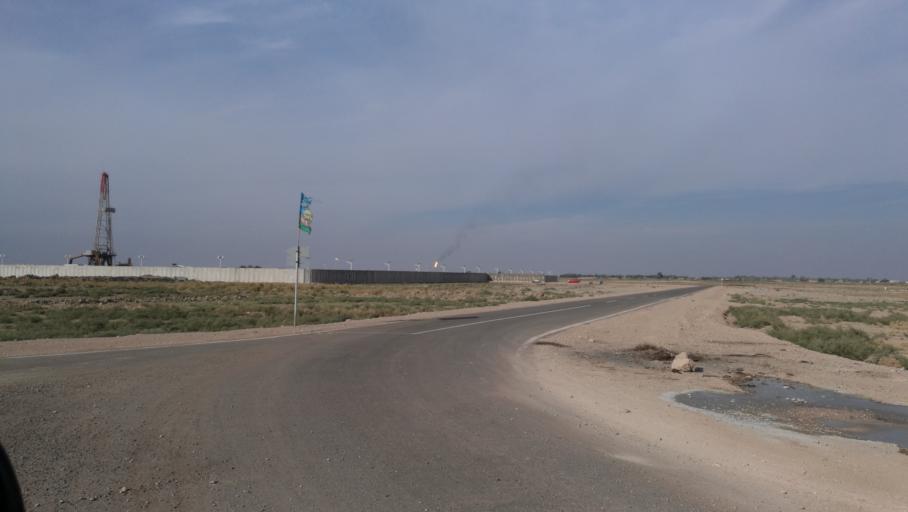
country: IQ
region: Dhi Qar
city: Ar Rifa`i
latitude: 31.7344
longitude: 46.0630
